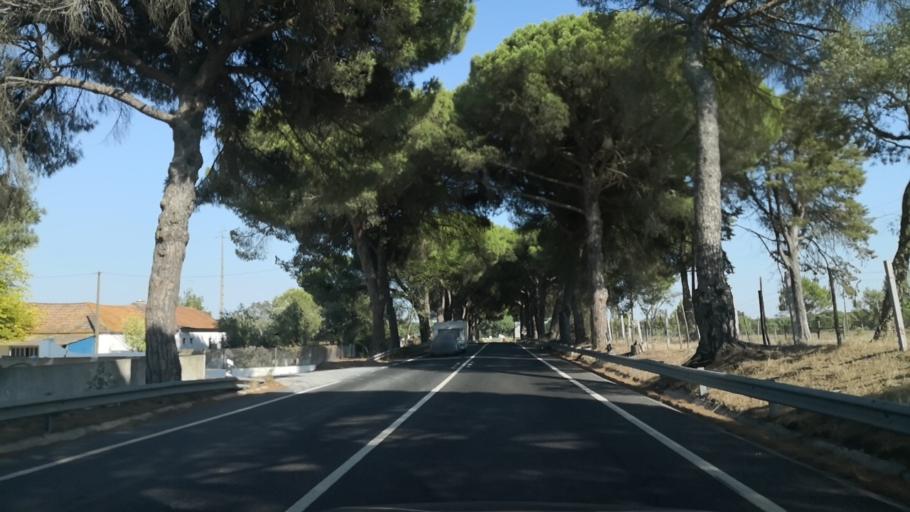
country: PT
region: Evora
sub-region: Vendas Novas
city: Vendas Novas
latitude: 38.7184
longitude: -8.6232
